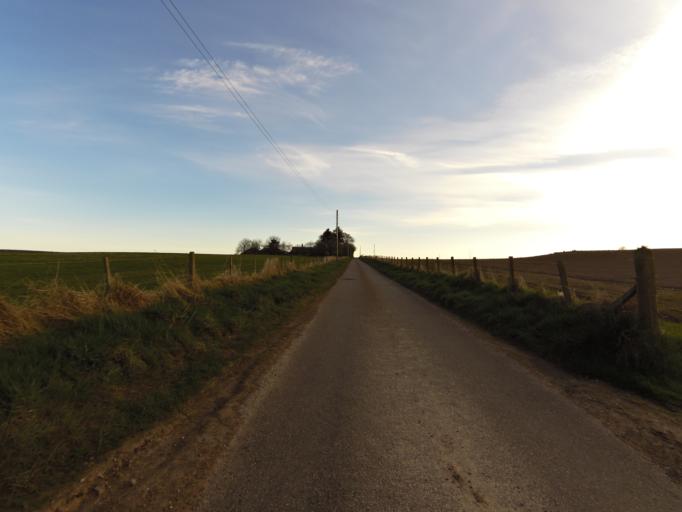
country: GB
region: Scotland
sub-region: Aberdeenshire
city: Stonehaven
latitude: 56.9385
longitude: -2.2226
